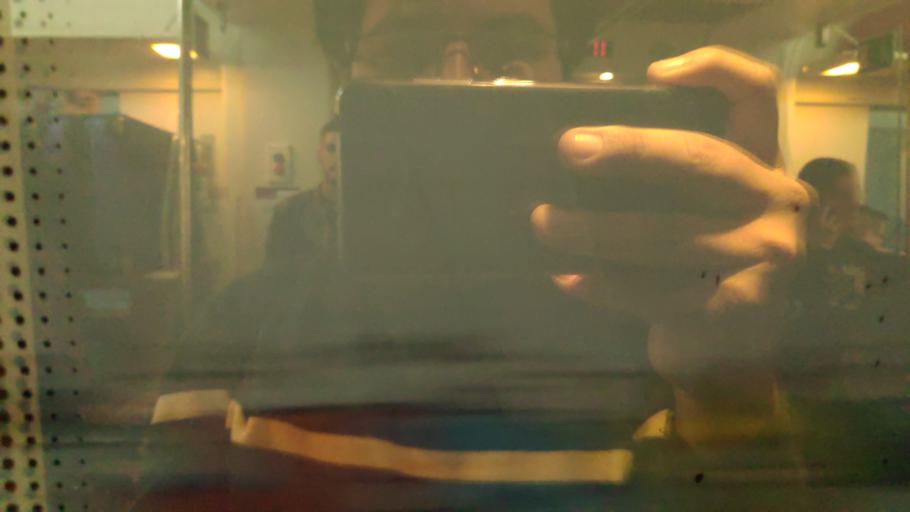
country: ES
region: Valencia
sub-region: Provincia de Castello
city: Benicassim
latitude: 40.0350
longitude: 0.0251
